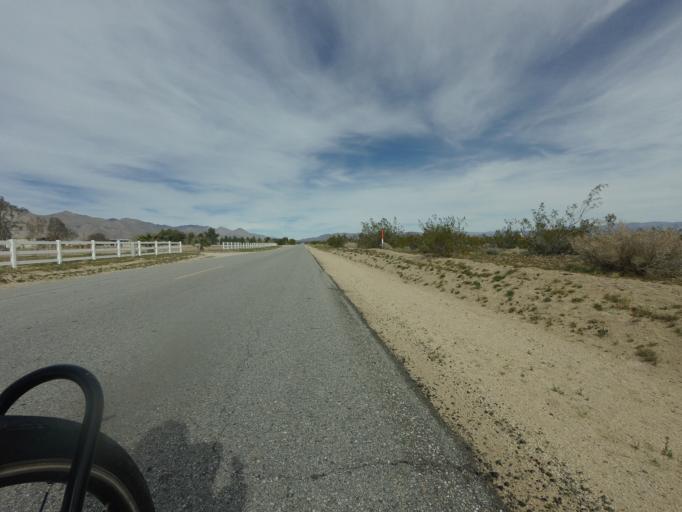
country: US
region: California
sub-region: Kern County
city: Inyokern
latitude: 35.7585
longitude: -117.8455
